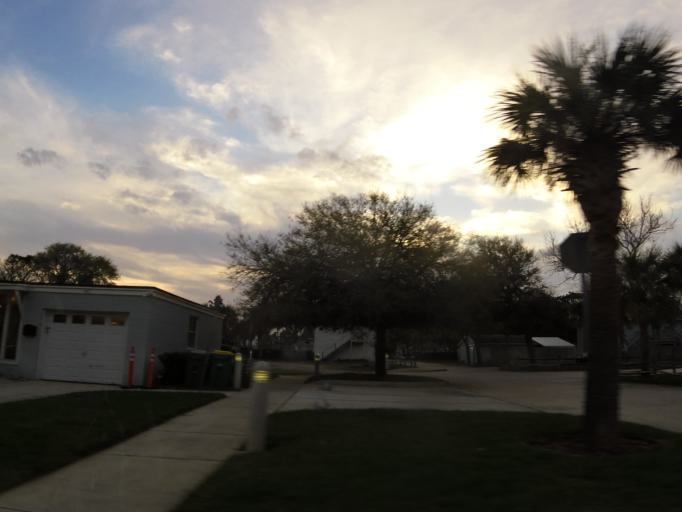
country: US
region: Florida
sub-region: Duval County
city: Jacksonville Beach
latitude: 30.2959
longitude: -81.3946
